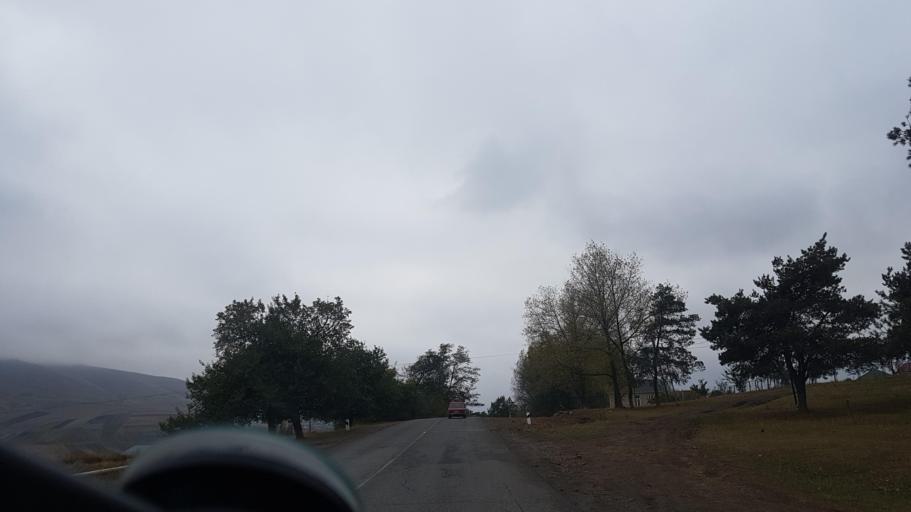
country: AZ
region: Gadabay Rayon
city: Ariqdam
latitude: 40.6486
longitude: 45.8104
